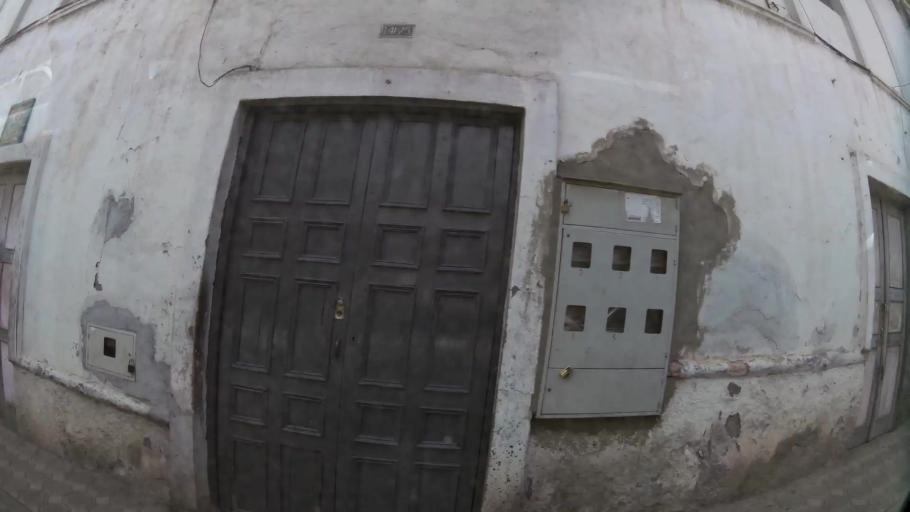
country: EC
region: Azuay
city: Cuenca
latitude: -2.8914
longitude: -79.0029
